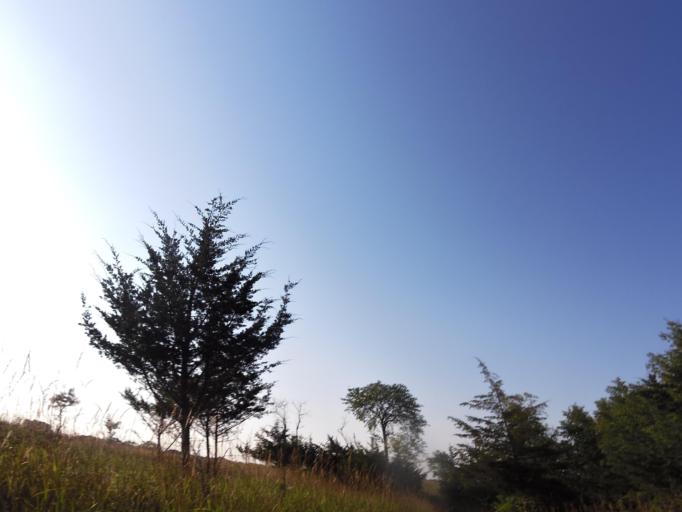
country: US
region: Minnesota
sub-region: Washington County
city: Afton
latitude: 44.8503
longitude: -92.7744
